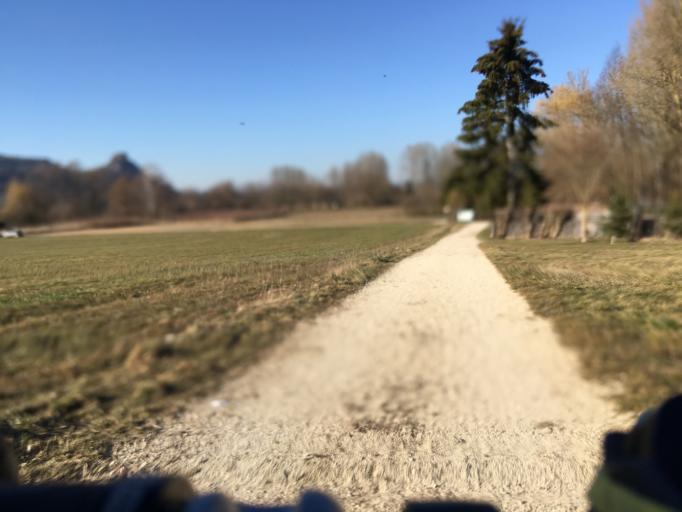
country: DE
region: Baden-Wuerttemberg
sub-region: Freiburg Region
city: Singen
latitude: 47.7811
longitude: 8.8394
